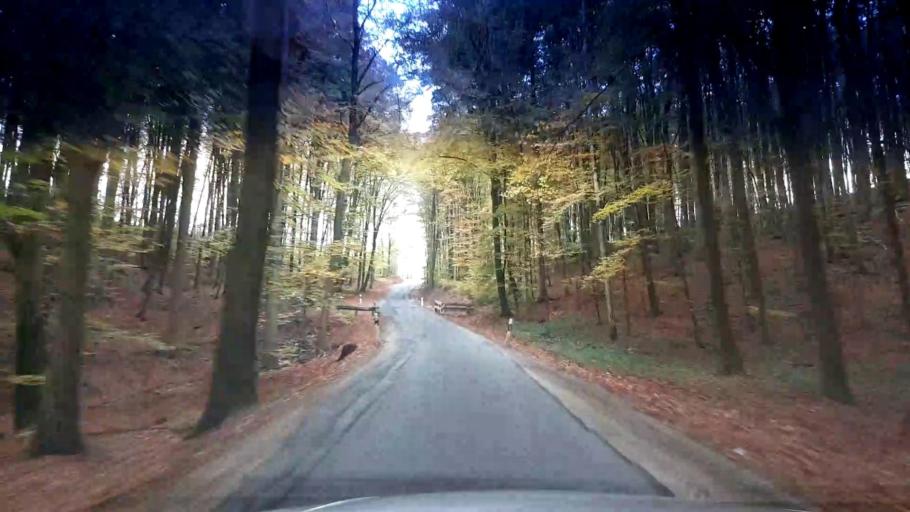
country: DE
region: Bavaria
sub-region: Upper Franconia
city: Priesendorf
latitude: 49.9098
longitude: 10.7417
